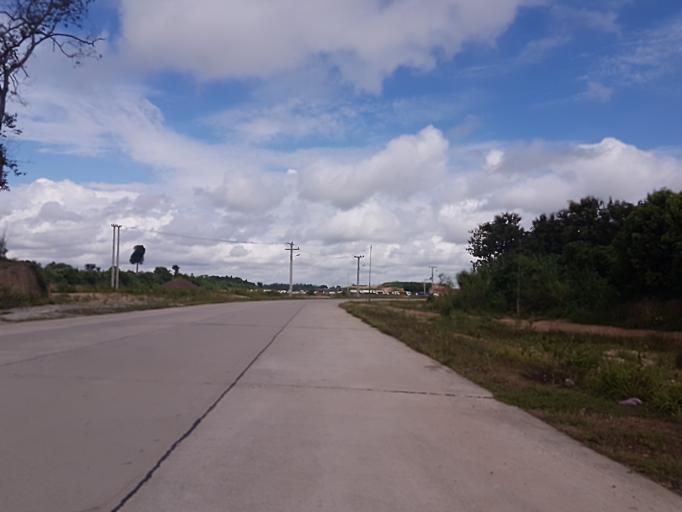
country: TH
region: Nong Khai
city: Nong Khai
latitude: 17.9104
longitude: 102.7080
